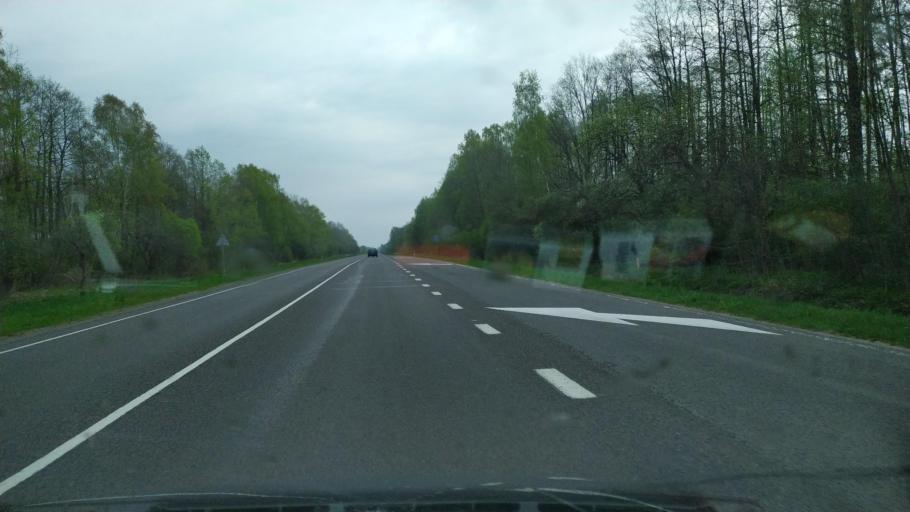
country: BY
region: Brest
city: Horad Kobryn
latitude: 52.3128
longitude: 24.5440
